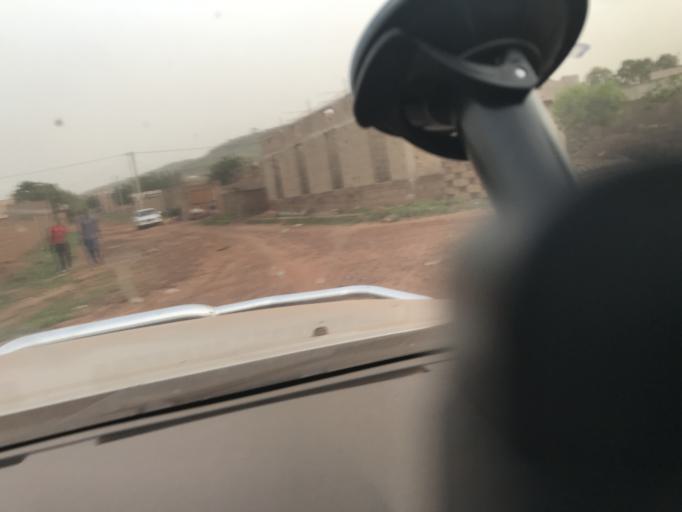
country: ML
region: Bamako
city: Bamako
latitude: 12.6517
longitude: -7.8822
